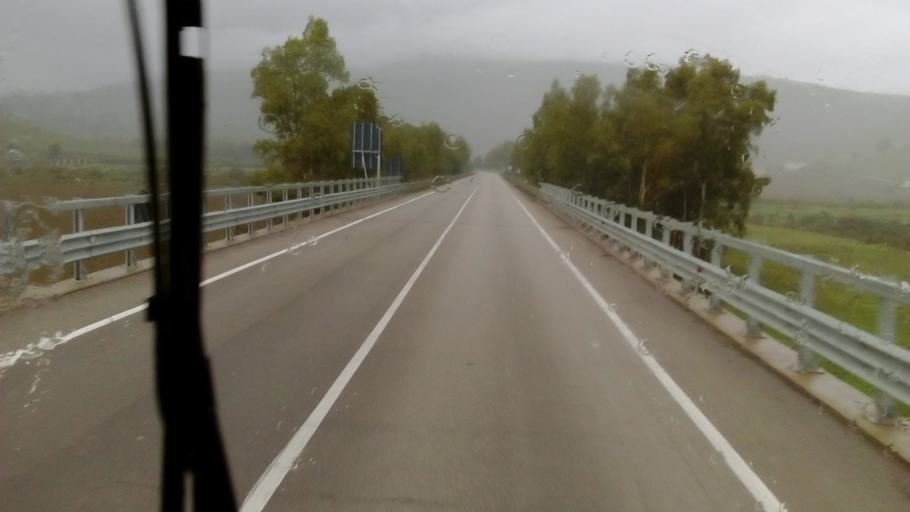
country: IT
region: Sicily
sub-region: Enna
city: Villarosa
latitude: 37.5300
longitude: 14.1293
